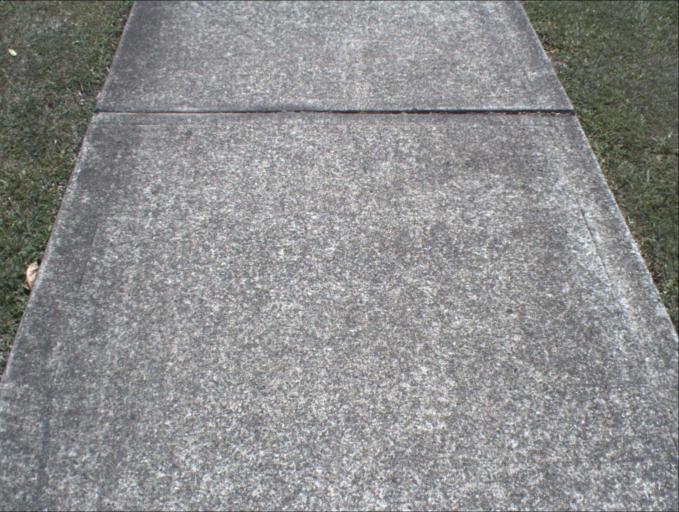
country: AU
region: Queensland
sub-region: Gold Coast
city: Yatala
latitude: -27.7258
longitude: 153.2122
